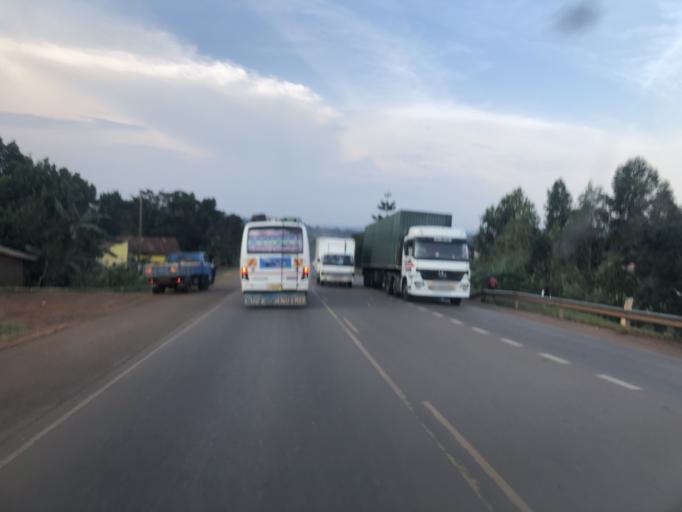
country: UG
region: Central Region
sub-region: Mpigi District
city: Mpigi
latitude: 0.2464
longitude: 32.3829
